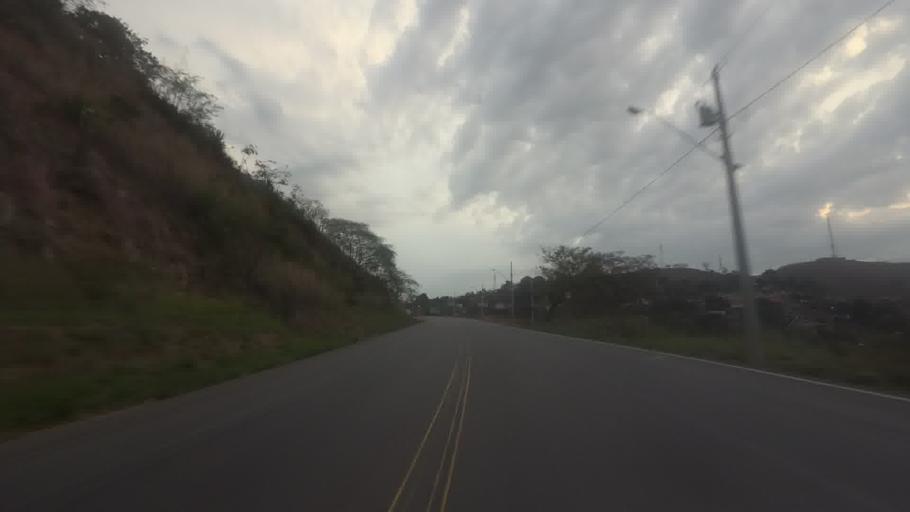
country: BR
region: Minas Gerais
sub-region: Alem Paraiba
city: Alem Paraiba
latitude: -21.8626
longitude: -42.6715
